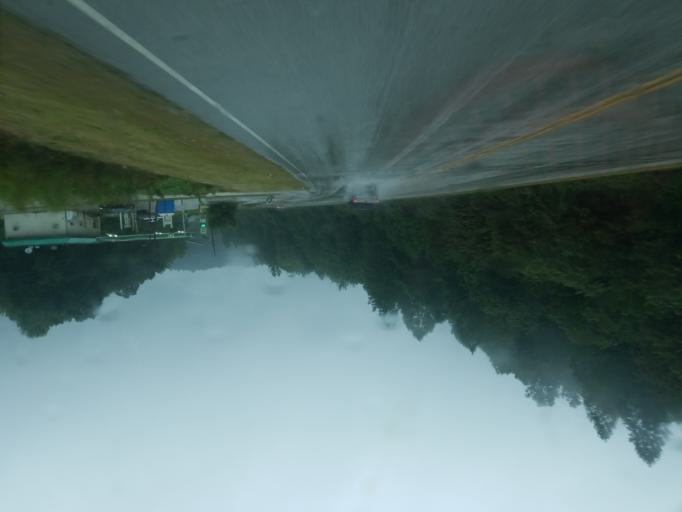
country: US
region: Kentucky
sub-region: Carter County
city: Olive Hill
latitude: 38.3251
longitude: -83.2080
